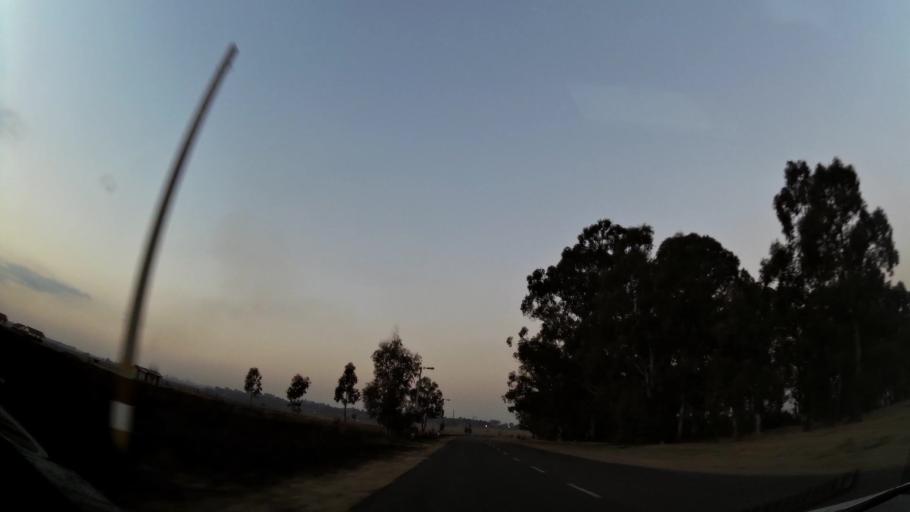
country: ZA
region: Gauteng
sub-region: Ekurhuleni Metropolitan Municipality
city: Nigel
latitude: -26.3532
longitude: 28.4475
